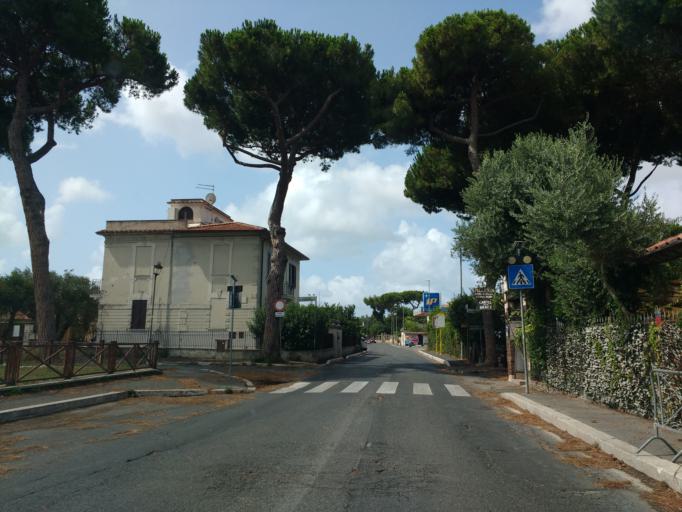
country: IT
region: Latium
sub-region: Citta metropolitana di Roma Capitale
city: Acilia-Castel Fusano-Ostia Antica
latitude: 41.7583
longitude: 12.3000
